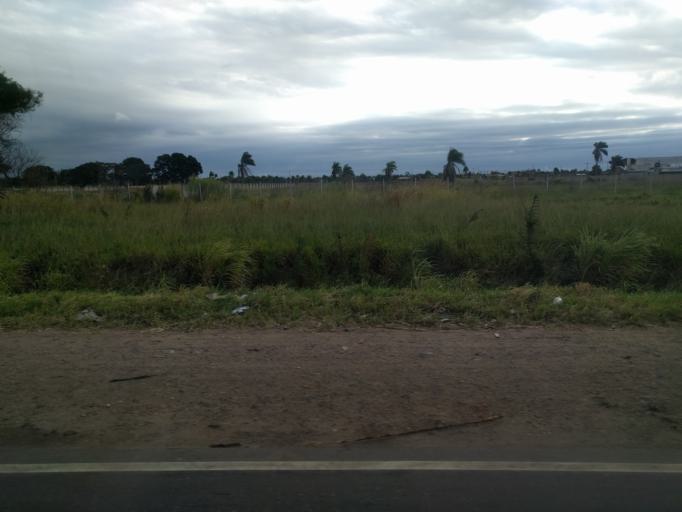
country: BO
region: Santa Cruz
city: La Belgica
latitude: -17.5900
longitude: -63.1584
